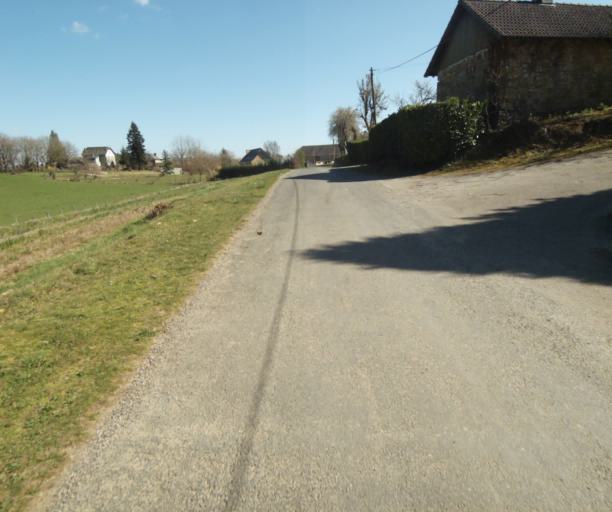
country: FR
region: Limousin
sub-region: Departement de la Correze
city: Saint-Mexant
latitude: 45.2916
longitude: 1.6801
